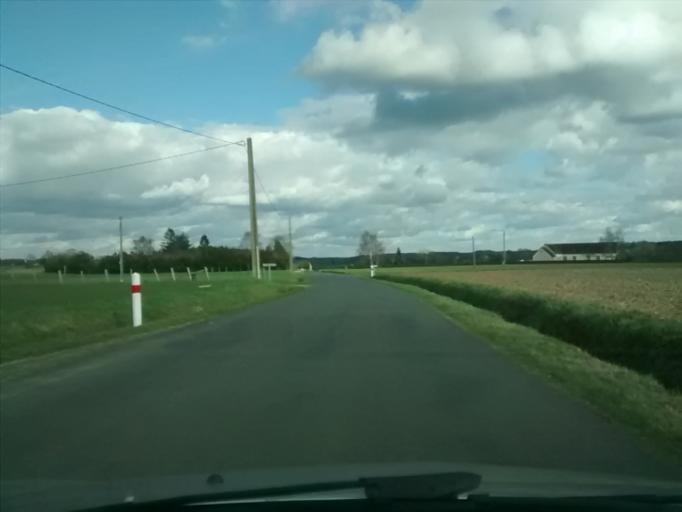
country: FR
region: Pays de la Loire
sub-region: Departement de la Sarthe
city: Bouloire
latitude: 47.9649
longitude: 0.5397
